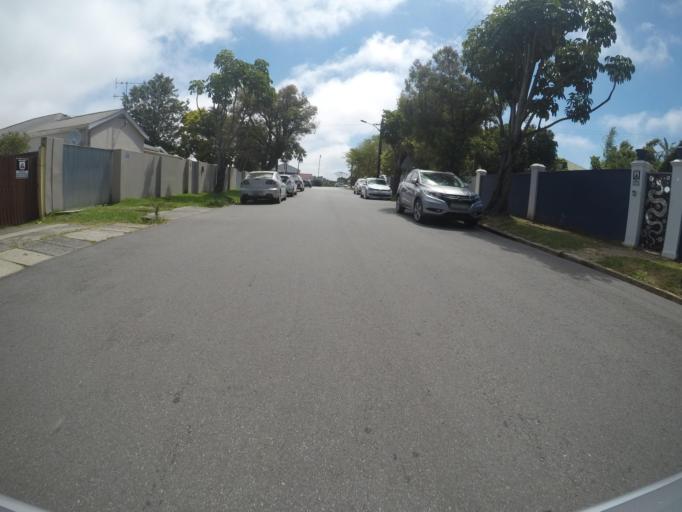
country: ZA
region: Eastern Cape
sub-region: Buffalo City Metropolitan Municipality
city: East London
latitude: -32.9748
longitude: 27.9004
